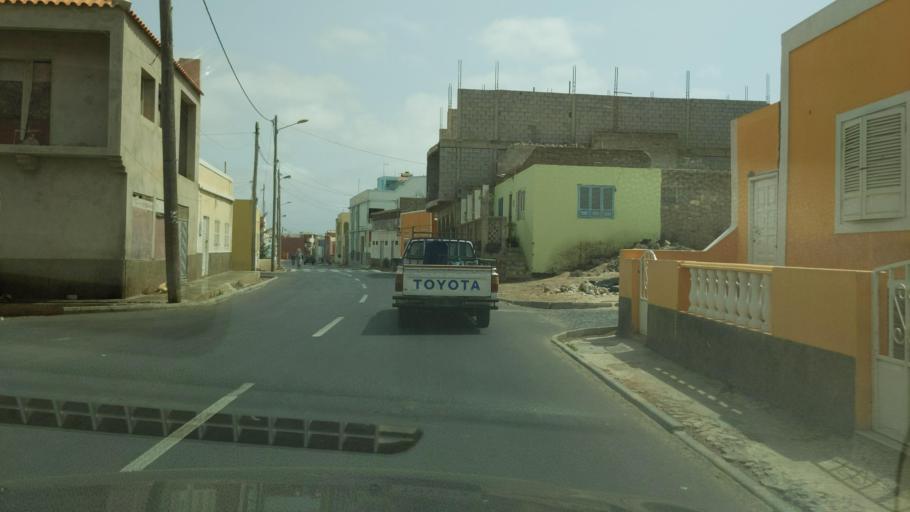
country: CV
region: Sal
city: Espargos
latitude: 16.7550
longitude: -22.9470
